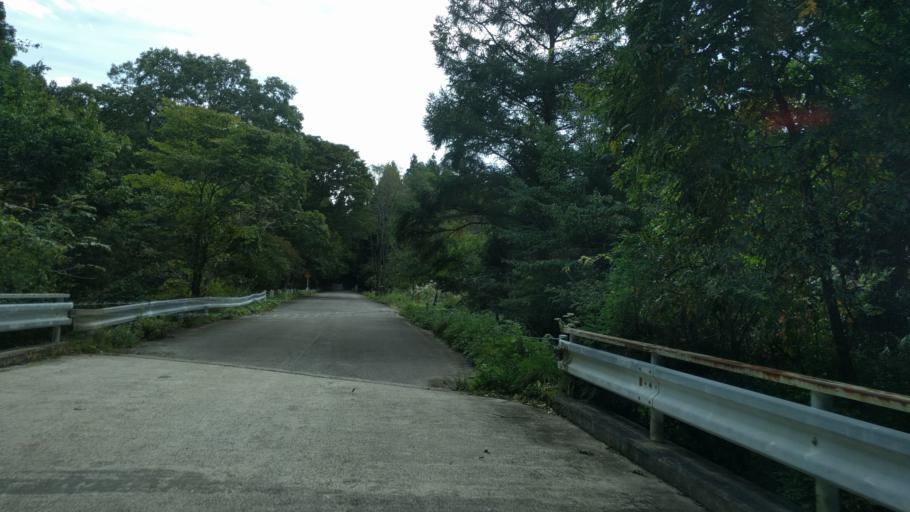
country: JP
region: Fukushima
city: Inawashiro
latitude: 37.3761
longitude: 140.1574
